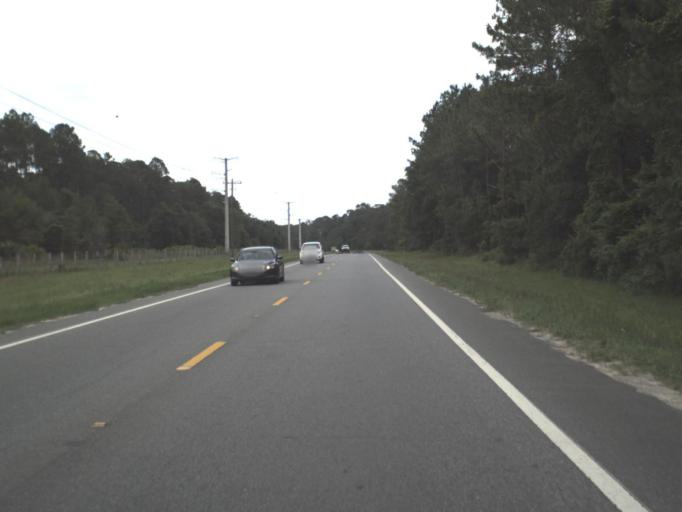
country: US
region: Florida
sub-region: Clay County
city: Keystone Heights
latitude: 29.8943
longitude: -81.9058
